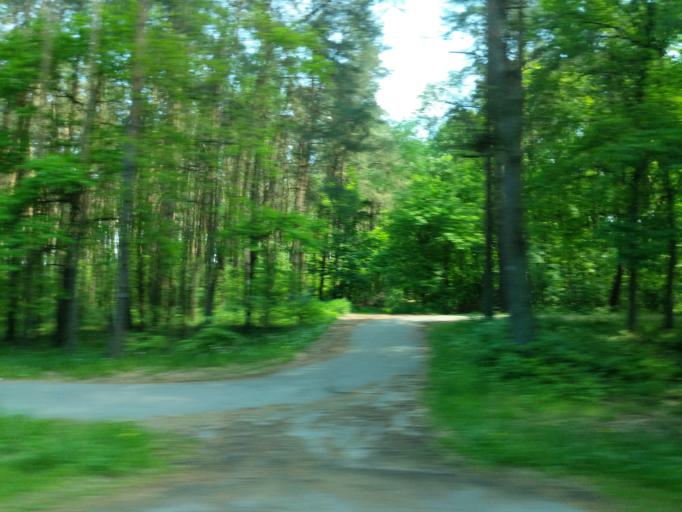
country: DE
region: Mecklenburg-Vorpommern
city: Stralendorf
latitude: 53.5018
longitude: 11.2893
